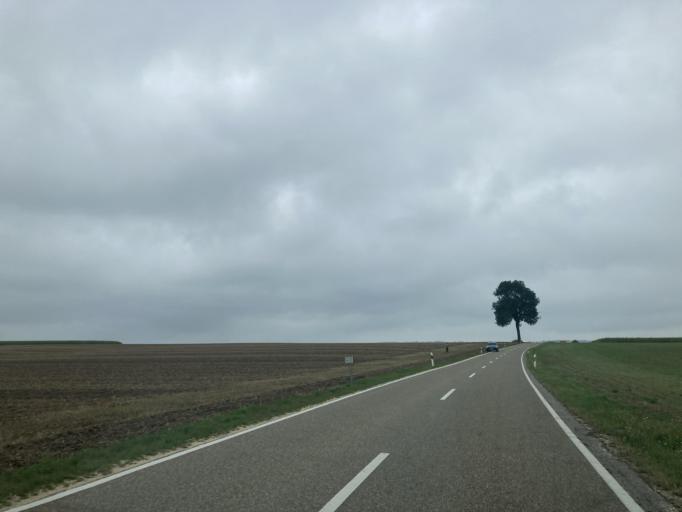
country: DE
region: Bavaria
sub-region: Swabia
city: Bachhagel
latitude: 48.6217
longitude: 10.3108
